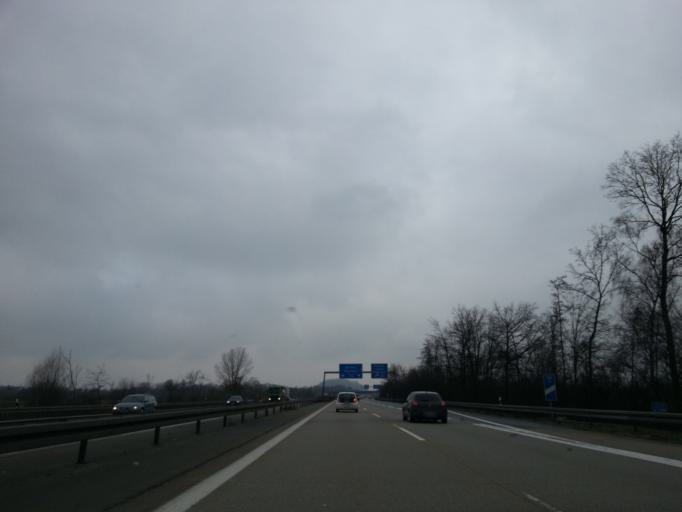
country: DE
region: Bavaria
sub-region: Lower Bavaria
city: Deggendorf
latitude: 48.8160
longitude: 12.9492
